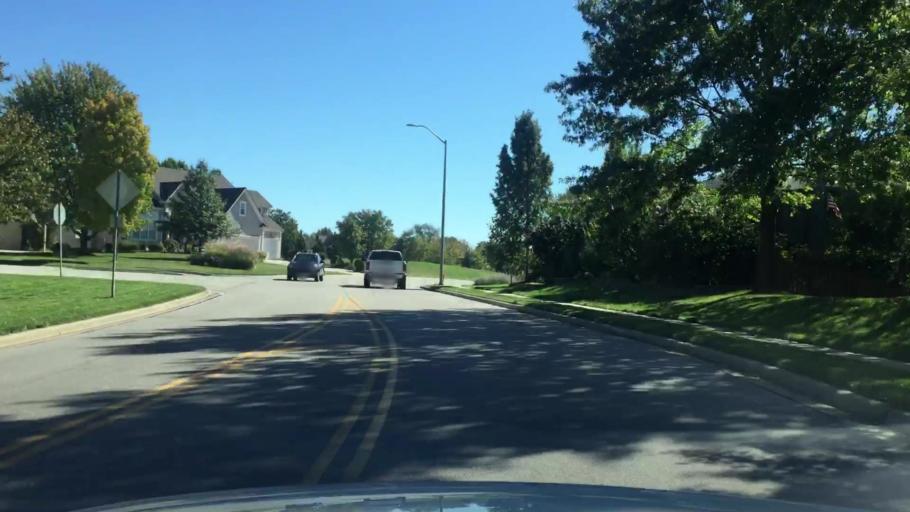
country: US
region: Kansas
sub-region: Johnson County
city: Shawnee
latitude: 39.0286
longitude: -94.7455
